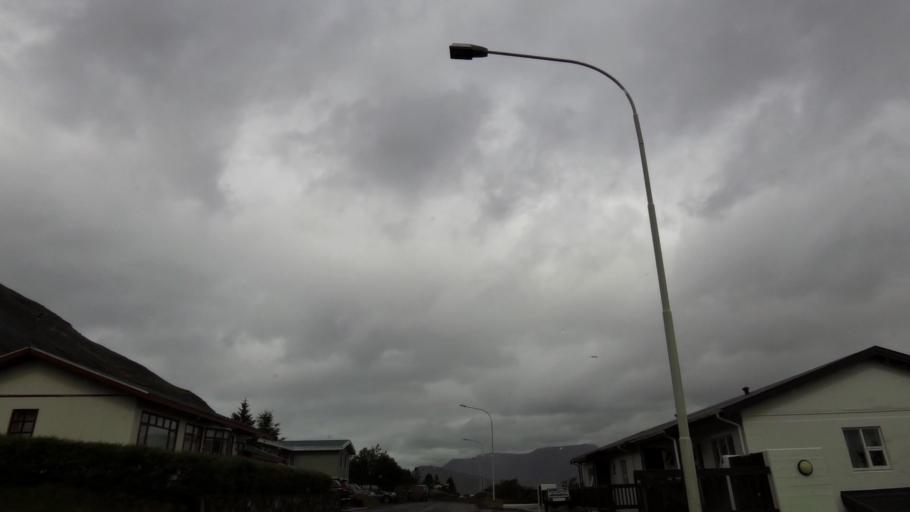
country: IS
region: Westfjords
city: Isafjoerdur
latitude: 65.8734
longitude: -23.4881
